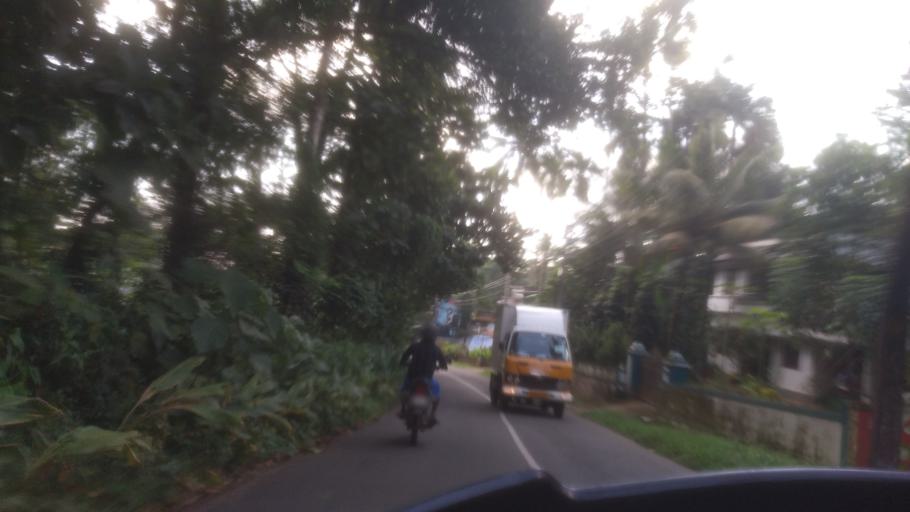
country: IN
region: Kerala
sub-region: Ernakulam
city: Kotamangalam
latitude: 10.0047
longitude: 76.6670
